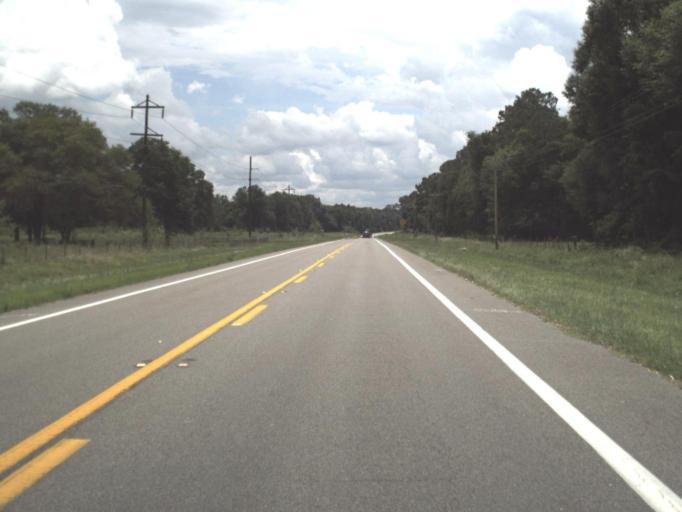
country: US
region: Florida
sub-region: Union County
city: Lake Butler
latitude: 30.0034
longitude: -82.2842
